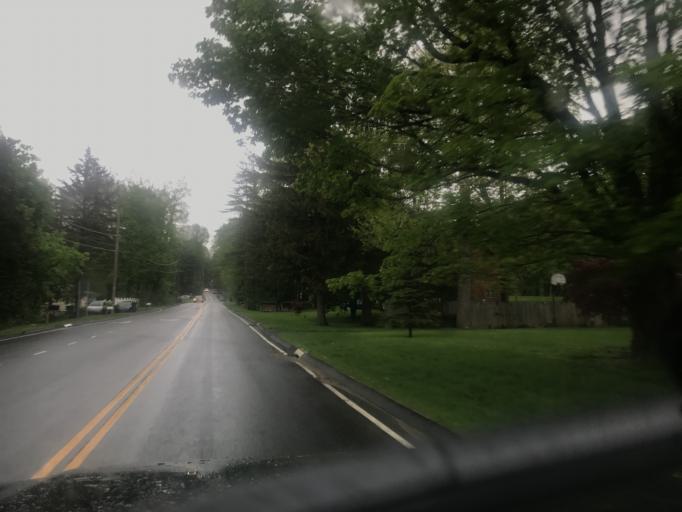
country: US
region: Connecticut
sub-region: Fairfield County
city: Bethel
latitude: 41.3861
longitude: -73.3981
